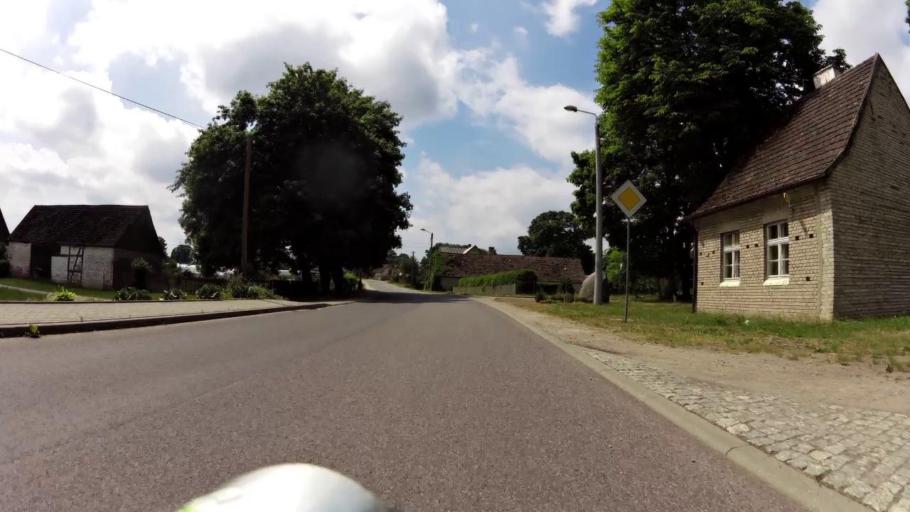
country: PL
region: West Pomeranian Voivodeship
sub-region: Powiat szczecinecki
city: Bialy Bor
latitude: 53.9494
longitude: 16.7780
